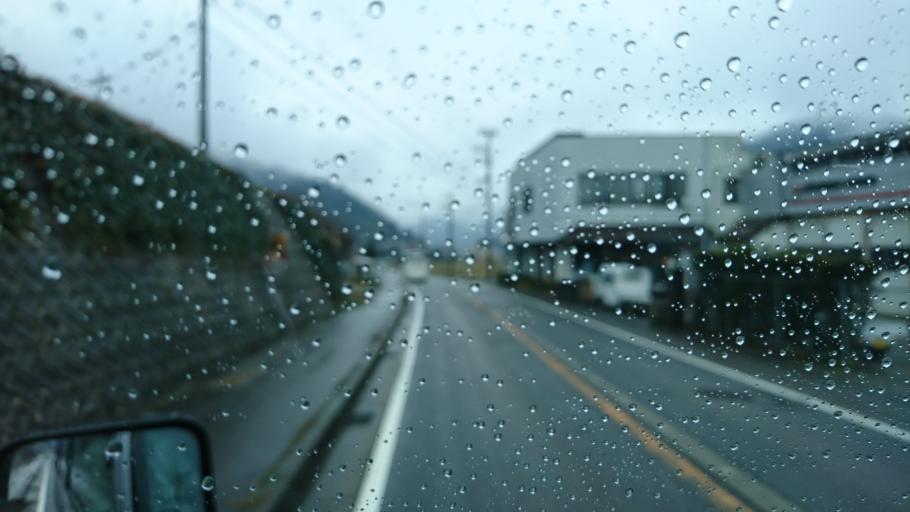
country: JP
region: Tottori
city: Tottori
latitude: 35.5730
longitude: 134.4879
